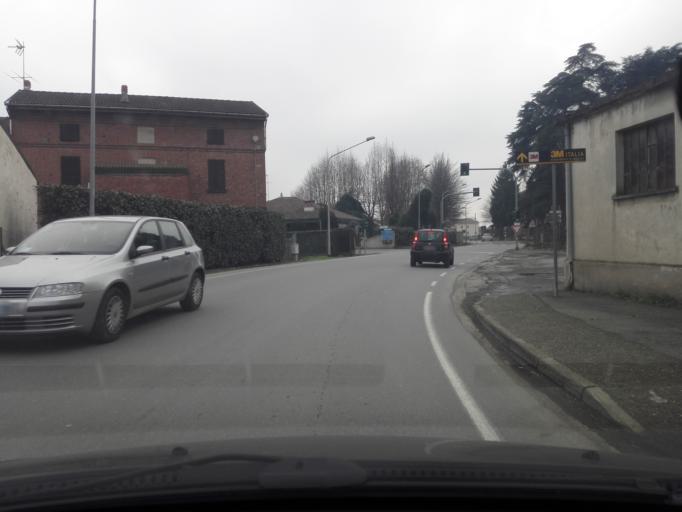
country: IT
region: Piedmont
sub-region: Provincia di Alessandria
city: Casal Cermelli
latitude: 44.8357
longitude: 8.6263
